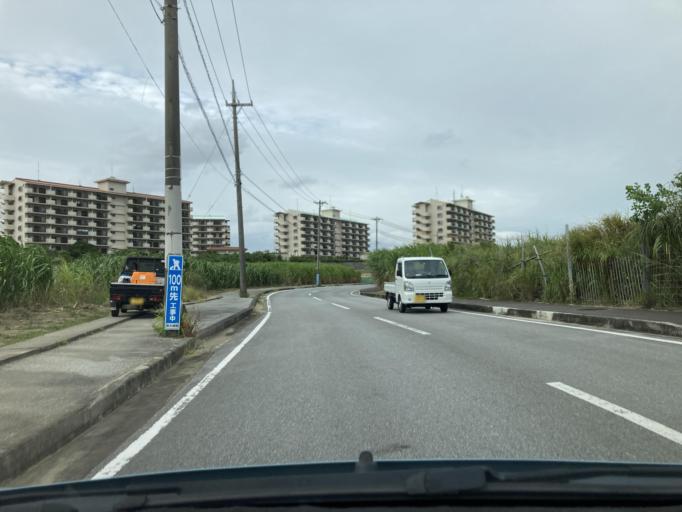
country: JP
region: Okinawa
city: Itoman
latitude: 26.1501
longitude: 127.6955
